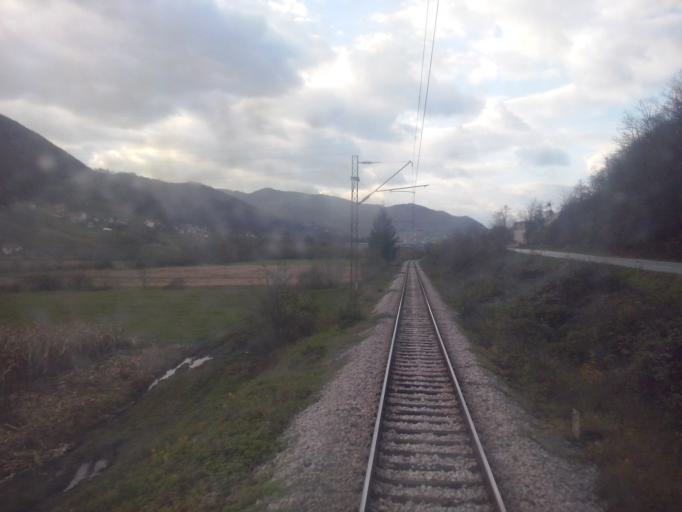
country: RS
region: Central Serbia
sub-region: Zlatiborski Okrug
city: Kosjeric
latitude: 43.9851
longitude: 19.9316
